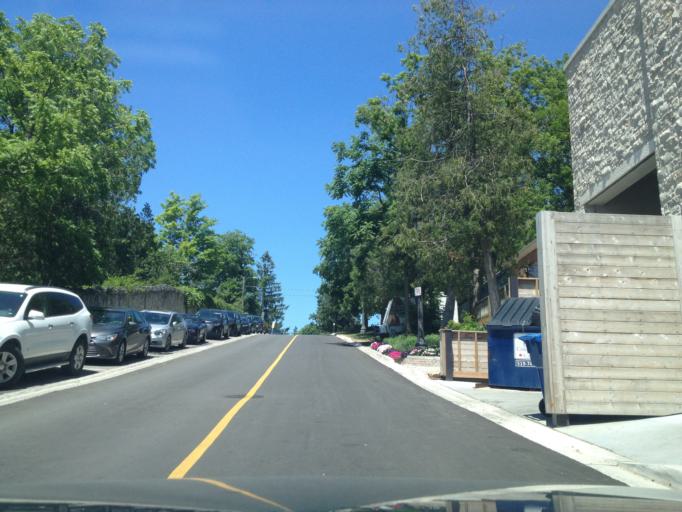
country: CA
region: Ontario
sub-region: Wellington County
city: Guelph
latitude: 43.6809
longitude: -80.4312
